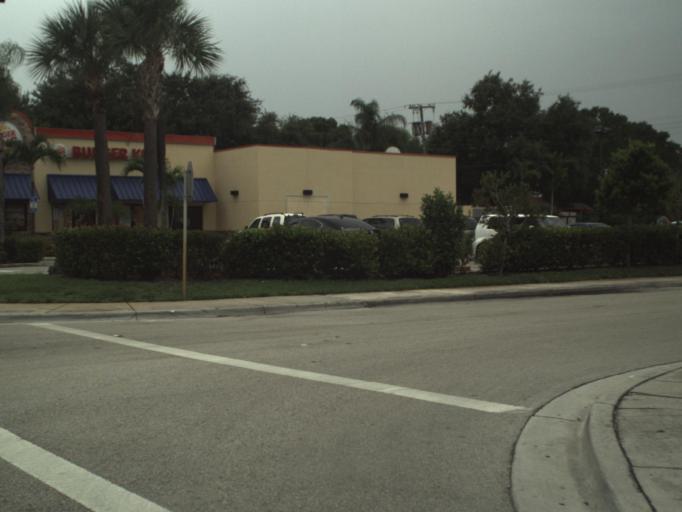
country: US
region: Florida
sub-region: Palm Beach County
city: Lake Worth
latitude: 26.6192
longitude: -80.0573
